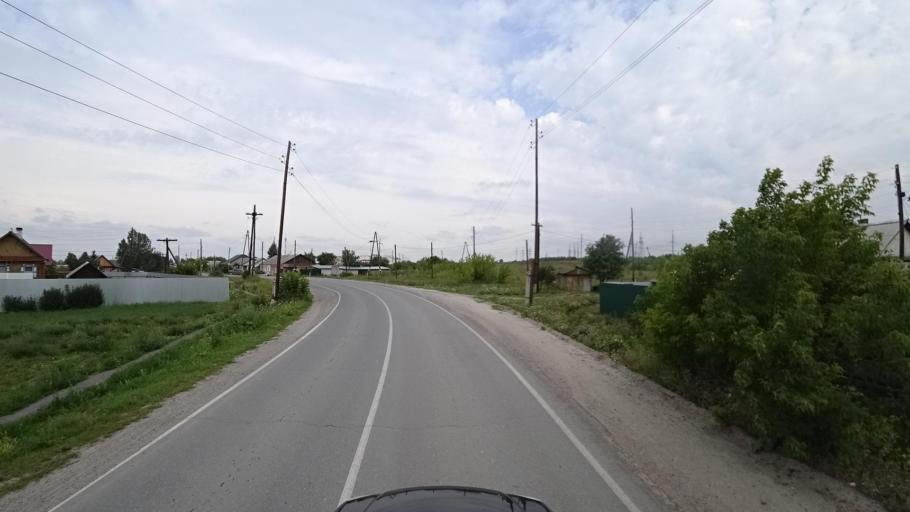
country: RU
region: Sverdlovsk
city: Kamyshlov
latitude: 56.8505
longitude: 62.7428
